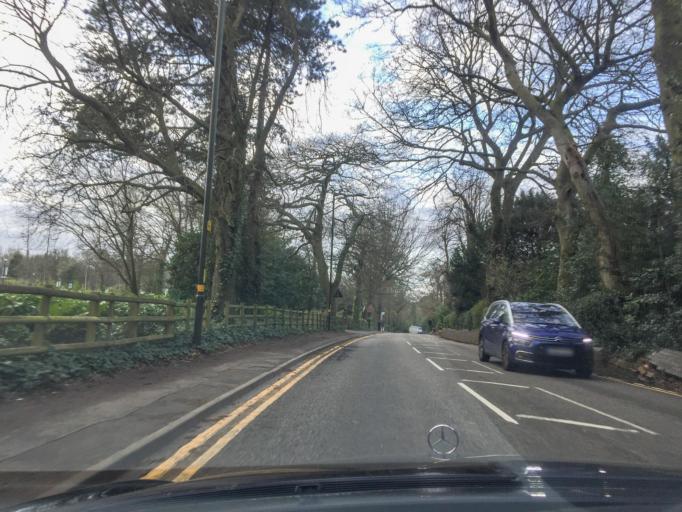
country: GB
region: England
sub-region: City and Borough of Birmingham
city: Birmingham
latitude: 52.4537
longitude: -1.9253
